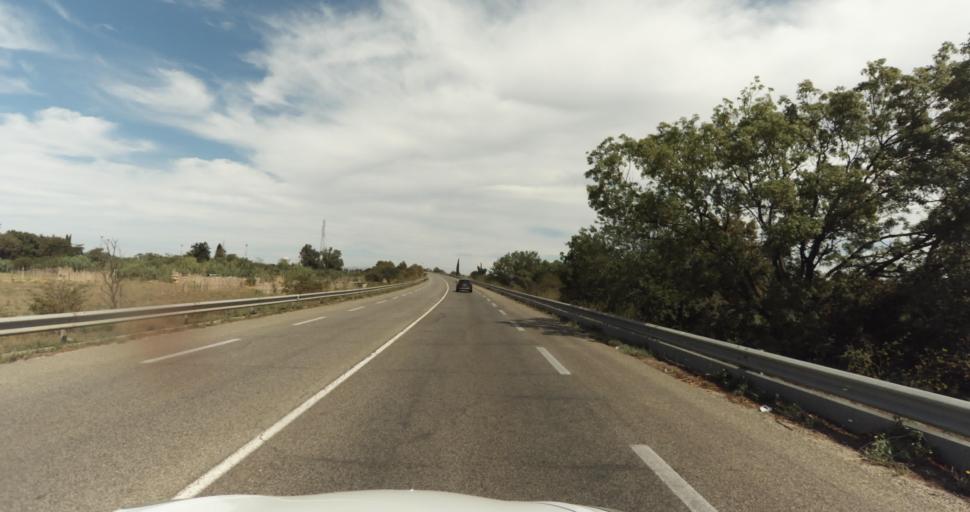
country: FR
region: Provence-Alpes-Cote d'Azur
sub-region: Departement des Bouches-du-Rhone
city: Miramas
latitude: 43.5754
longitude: 4.9842
